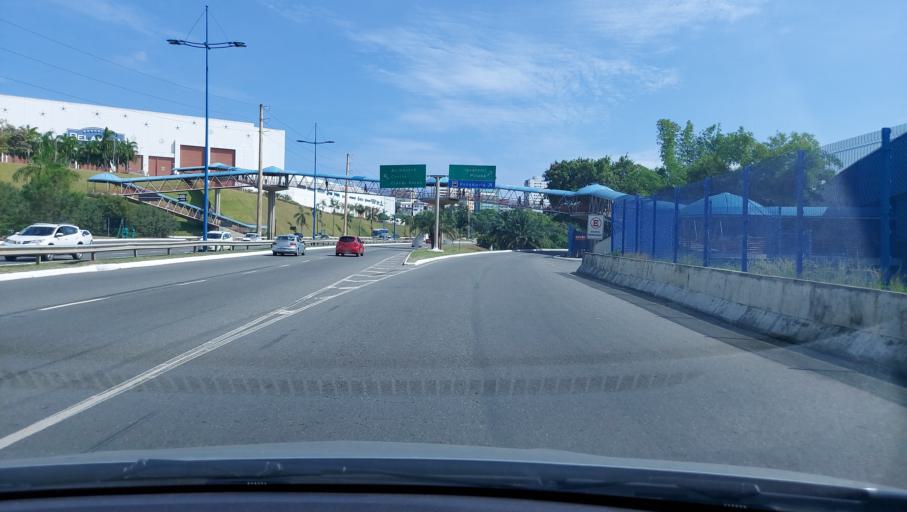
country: BR
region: Bahia
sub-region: Salvador
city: Salvador
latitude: -12.9684
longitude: -38.4766
